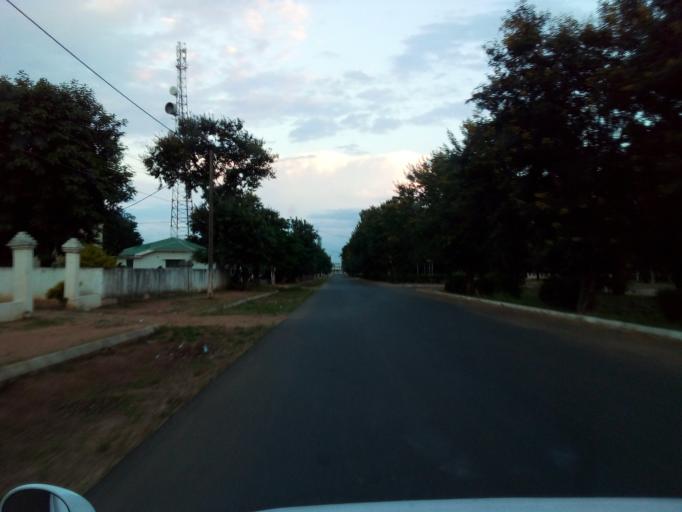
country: MZ
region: Maputo City
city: Maputo
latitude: -26.3428
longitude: 32.6748
